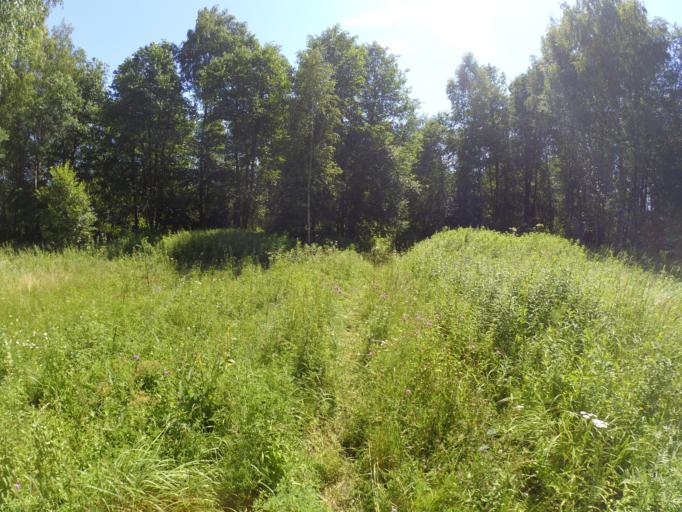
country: RU
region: Moskovskaya
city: Fosforitnyy
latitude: 55.3355
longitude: 38.9168
